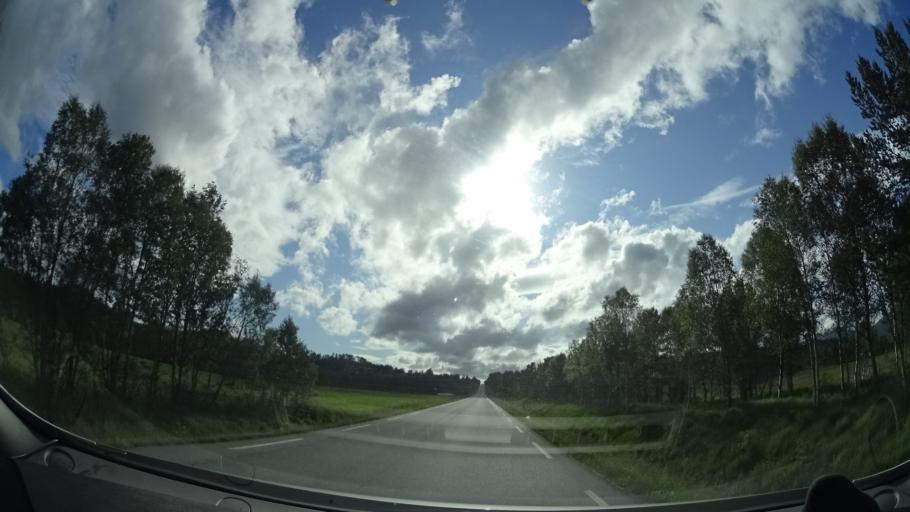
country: NO
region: More og Romsdal
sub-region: Halsa
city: Liaboen
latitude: 63.1266
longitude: 8.3662
